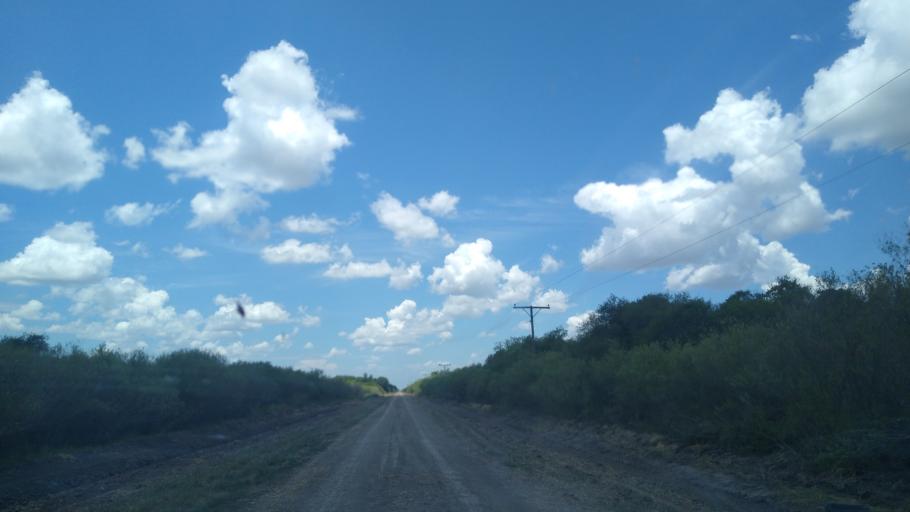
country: AR
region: Chaco
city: Presidencia Roque Saenz Pena
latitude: -26.7414
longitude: -60.3336
